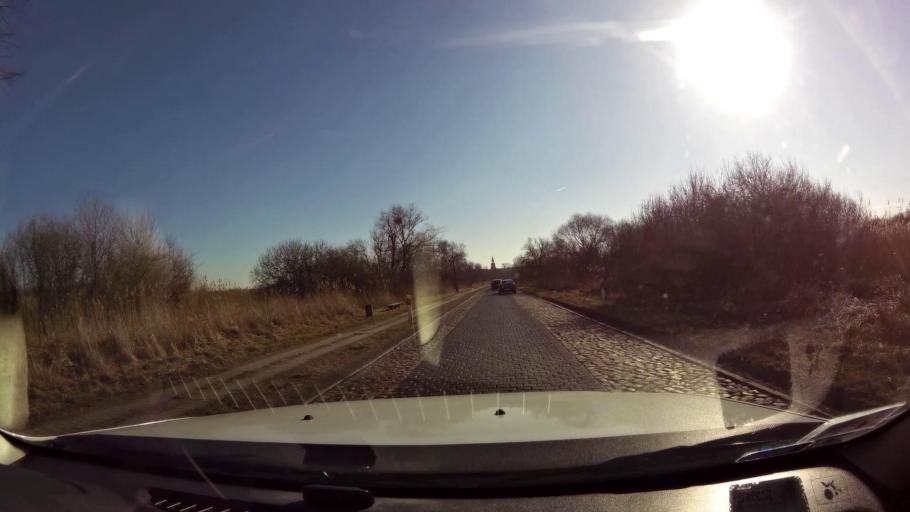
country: PL
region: West Pomeranian Voivodeship
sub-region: Powiat gryfinski
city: Gryfino
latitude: 53.2538
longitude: 14.4719
